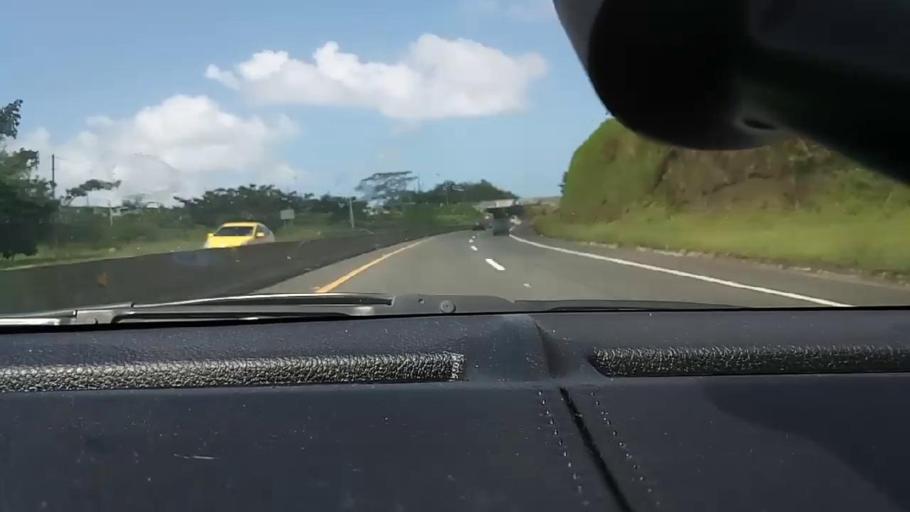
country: PA
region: Colon
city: Las Margaritas
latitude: 9.3293
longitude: -79.8733
